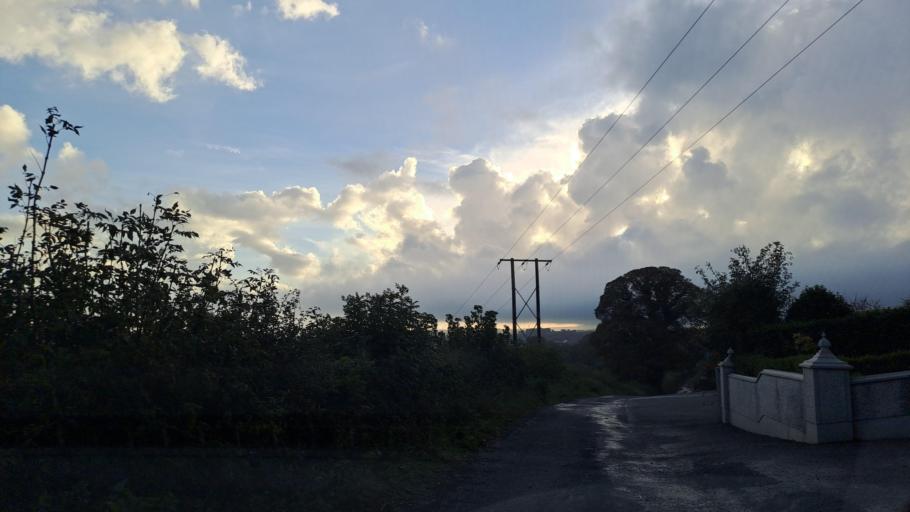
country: IE
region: Ulster
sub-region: County Monaghan
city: Carrickmacross
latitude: 53.9750
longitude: -6.7464
